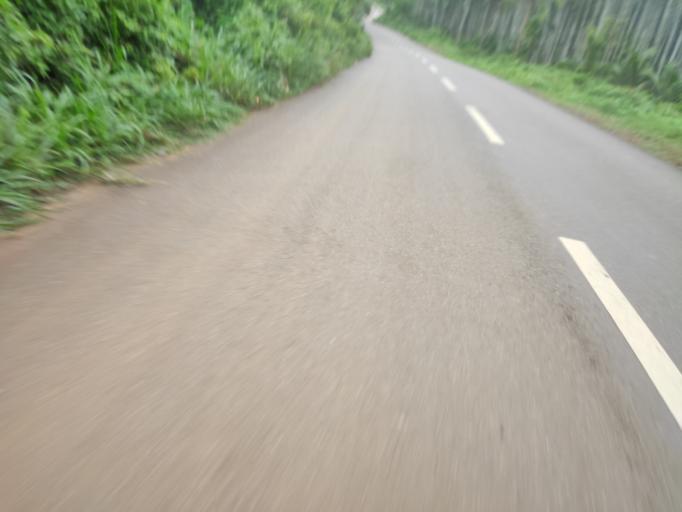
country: IN
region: Kerala
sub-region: Malappuram
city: Manjeri
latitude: 11.1657
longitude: 76.1719
